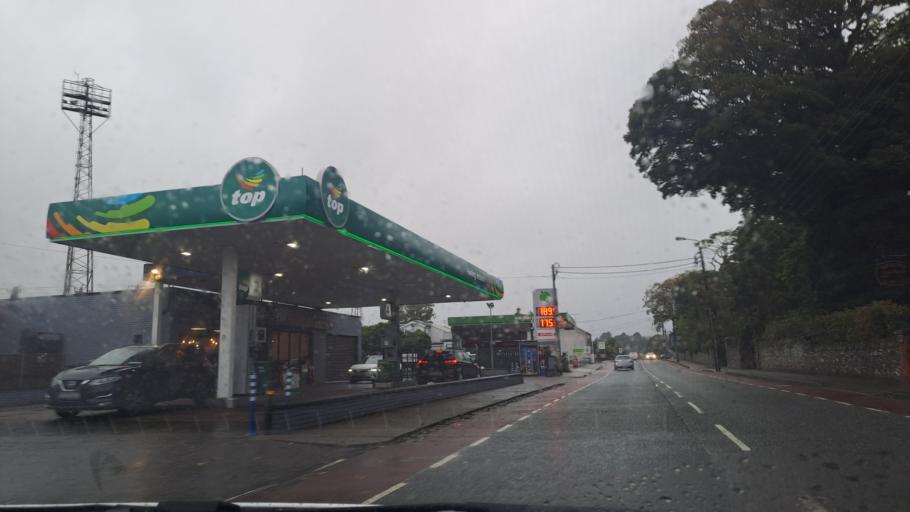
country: IE
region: Leinster
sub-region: Lu
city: Dundalk
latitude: 54.0000
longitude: -6.4148
